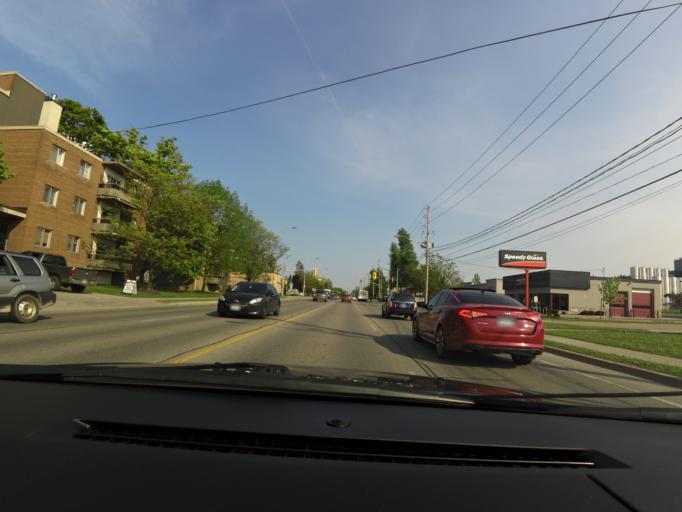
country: CA
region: Ontario
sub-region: Wellington County
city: Guelph
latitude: 43.5608
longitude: -80.2717
